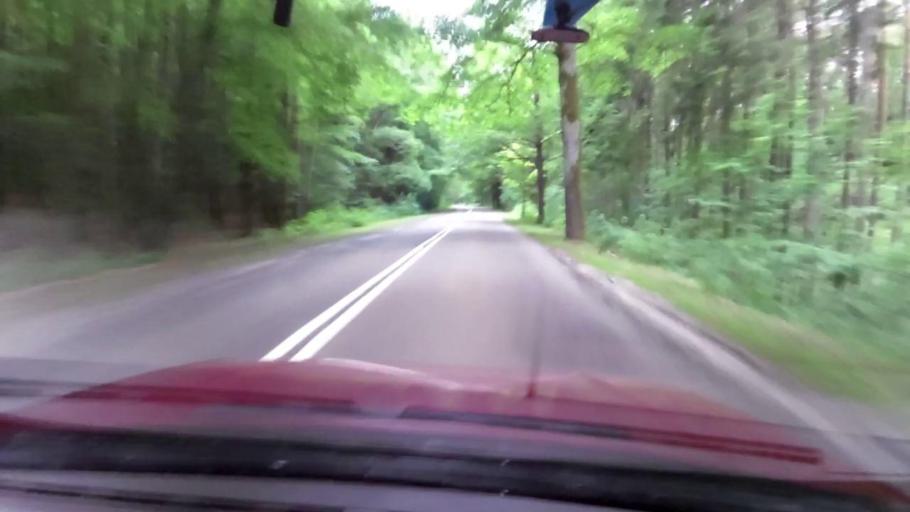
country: PL
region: West Pomeranian Voivodeship
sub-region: Powiat koszalinski
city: Sianow
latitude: 54.1894
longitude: 16.2891
